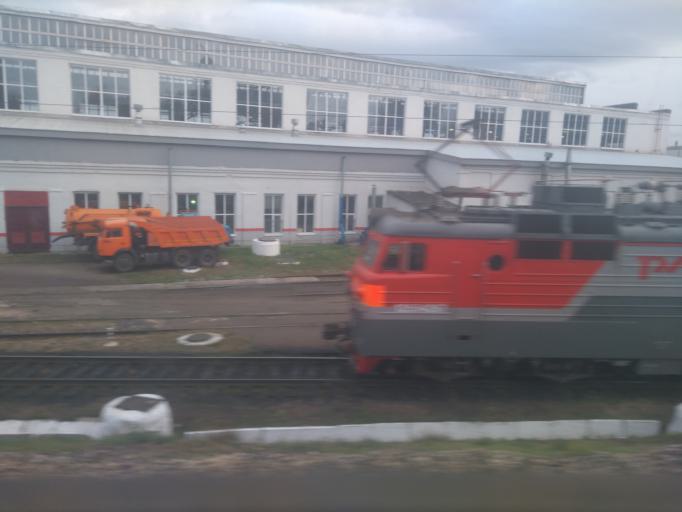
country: RU
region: Tatarstan
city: Osinovo
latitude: 55.8174
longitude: 48.8980
